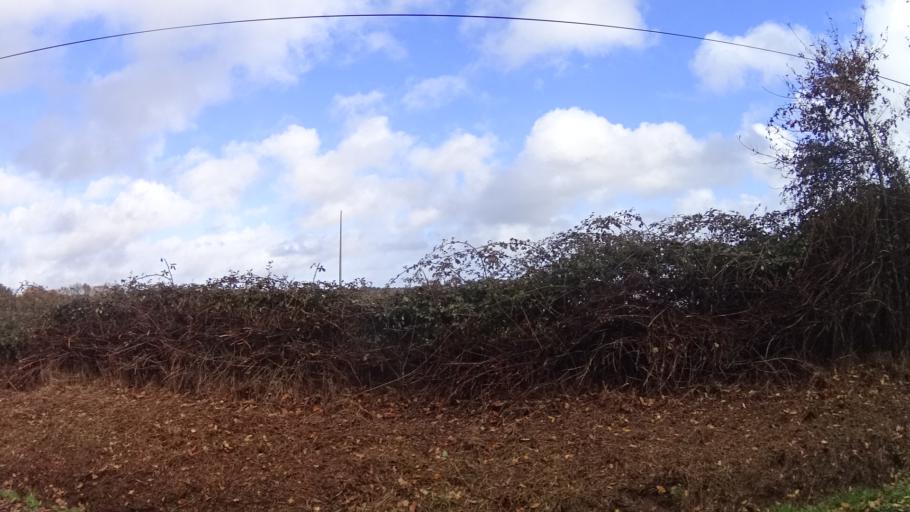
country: FR
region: Pays de la Loire
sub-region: Departement de la Loire-Atlantique
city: Fegreac
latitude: 47.6046
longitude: -2.0656
